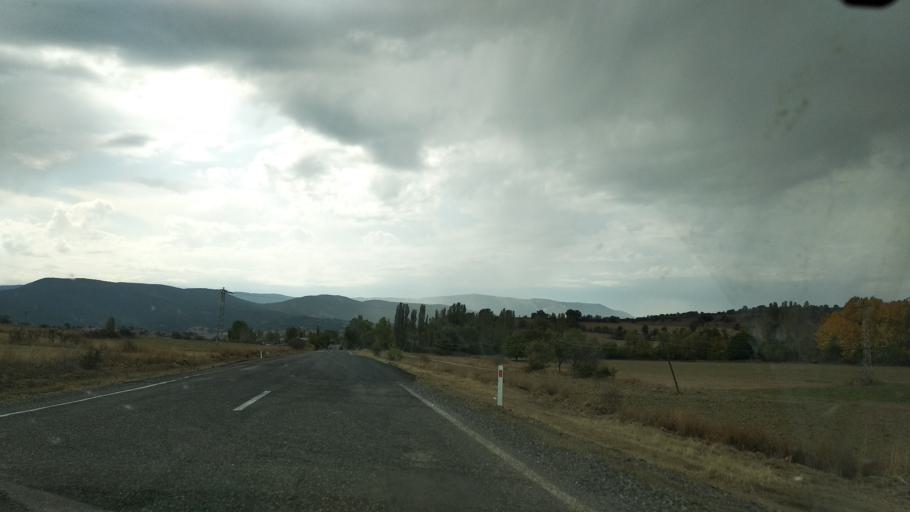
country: TR
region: Bolu
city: Seben
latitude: 40.3465
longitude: 31.4744
